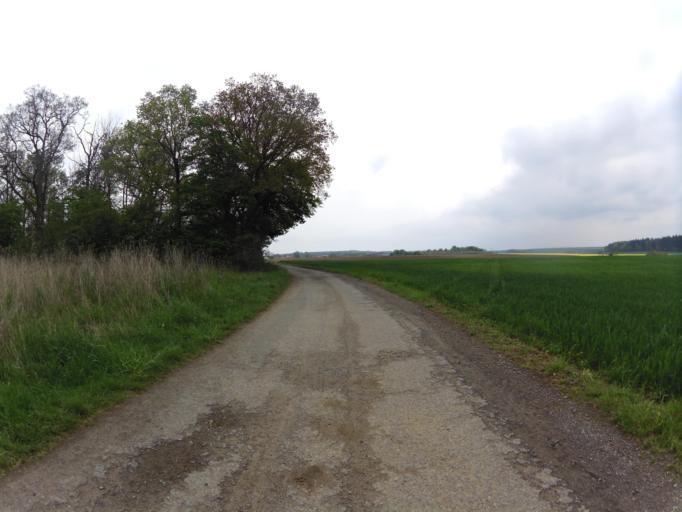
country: DE
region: Bavaria
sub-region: Regierungsbezirk Unterfranken
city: Frickenhausen
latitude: 49.7044
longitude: 10.0714
